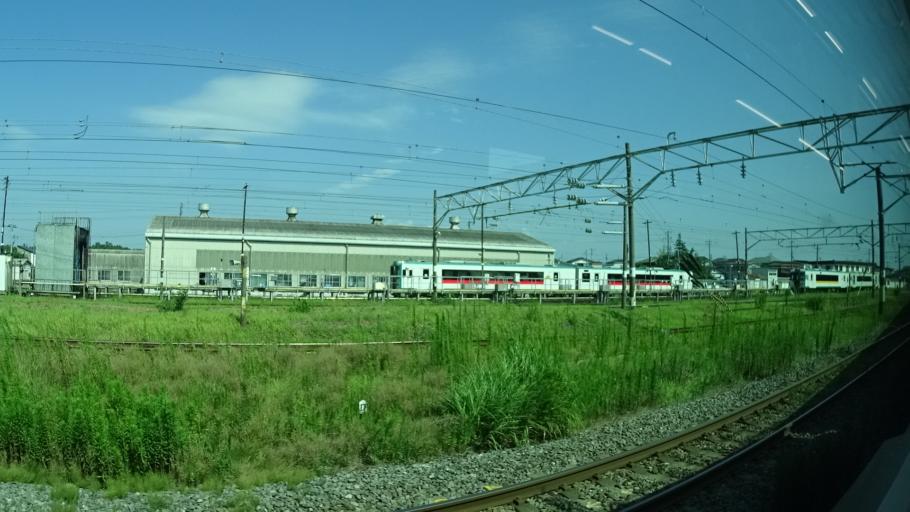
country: JP
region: Miyagi
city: Kogota
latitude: 38.5367
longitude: 141.0650
